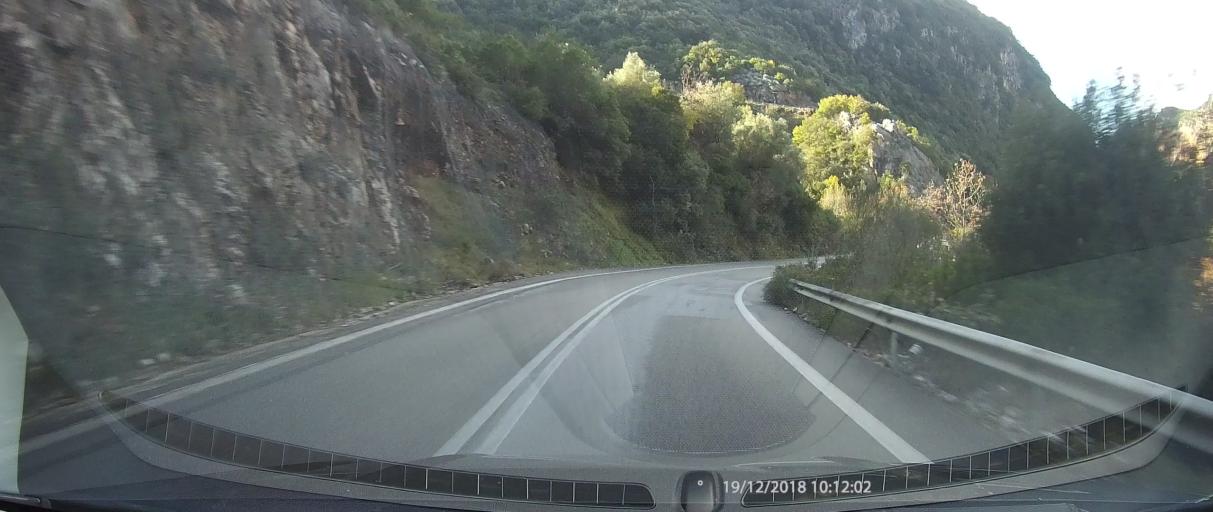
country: GR
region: Peloponnese
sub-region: Nomos Messinias
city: Kalamata
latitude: 37.0925
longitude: 22.1738
